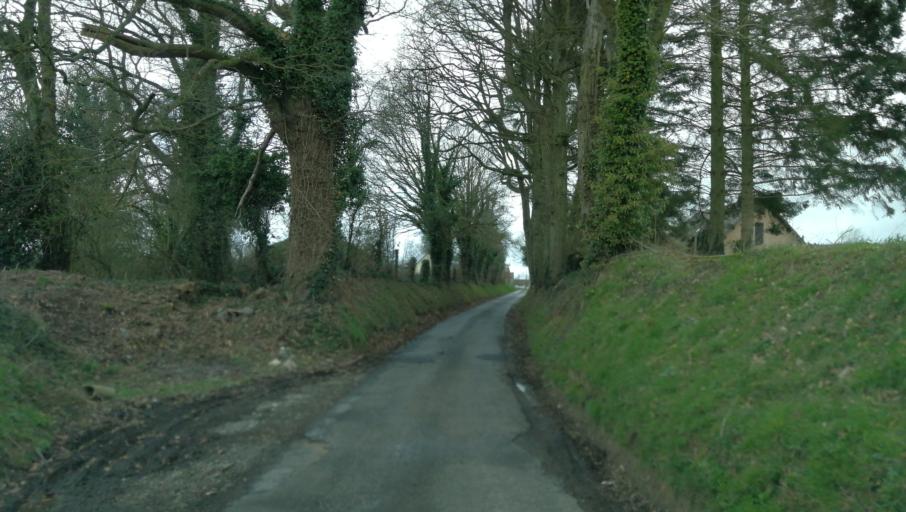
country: FR
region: Haute-Normandie
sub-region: Departement de l'Eure
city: Lieurey
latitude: 49.2358
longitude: 0.5096
